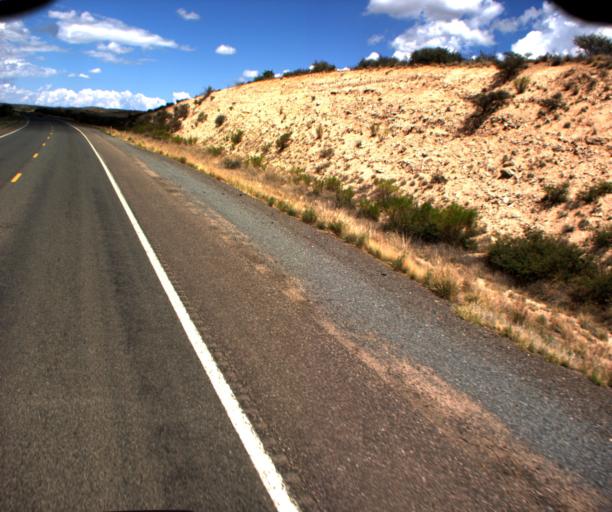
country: US
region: Arizona
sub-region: Yavapai County
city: Dewey-Humboldt
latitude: 34.5214
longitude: -112.0668
